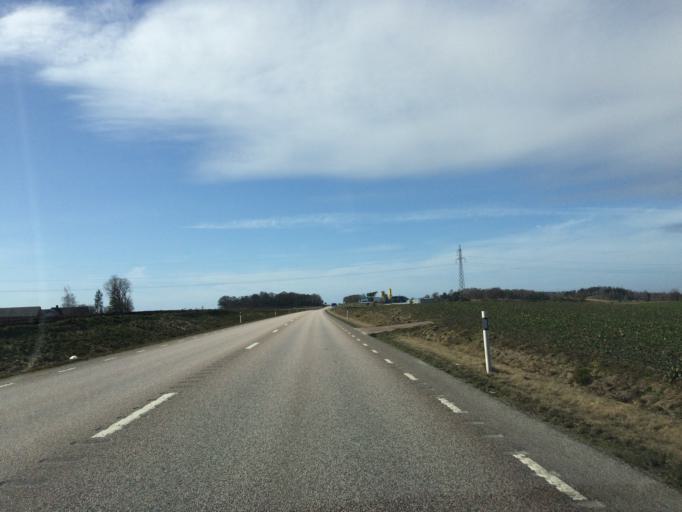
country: SE
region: Halland
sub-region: Laholms Kommun
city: Veinge
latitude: 56.5429
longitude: 13.1042
